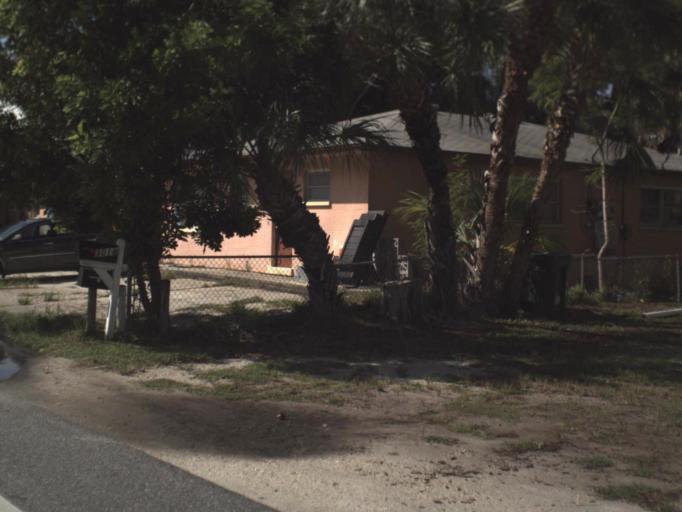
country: US
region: Florida
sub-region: Manatee County
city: Holmes Beach
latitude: 27.4905
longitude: -82.7072
